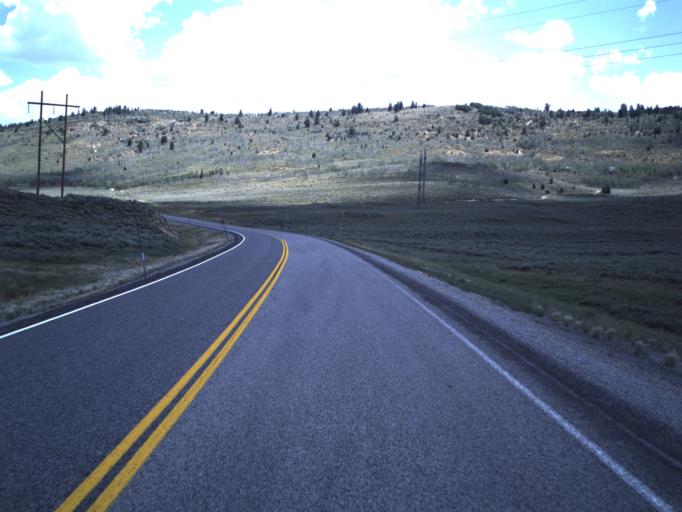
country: US
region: Utah
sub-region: Carbon County
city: Helper
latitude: 39.8335
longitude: -111.1323
